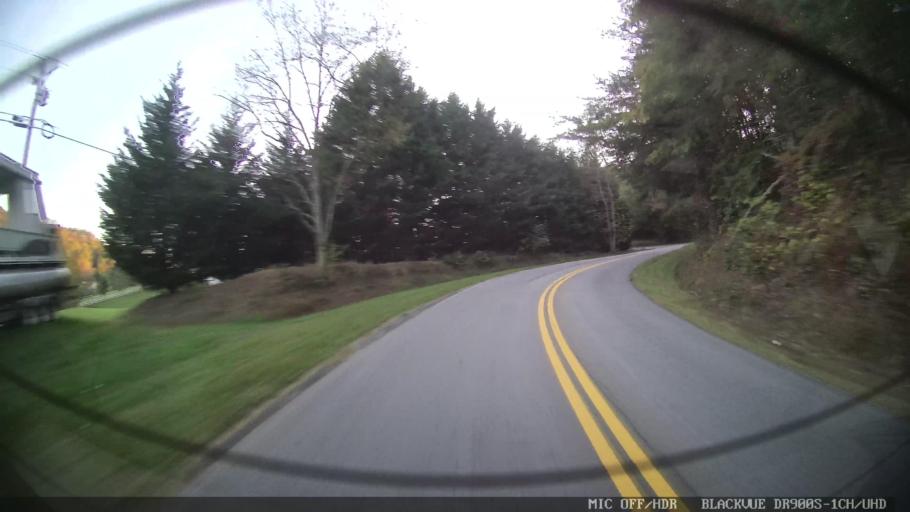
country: US
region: Georgia
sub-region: Union County
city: Blairsville
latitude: 34.8556
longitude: -83.8981
